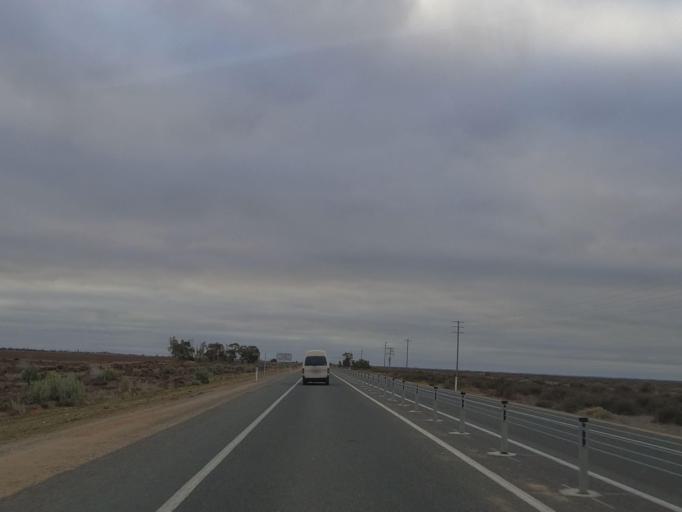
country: AU
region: Victoria
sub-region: Swan Hill
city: Swan Hill
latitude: -35.5198
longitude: 143.7307
